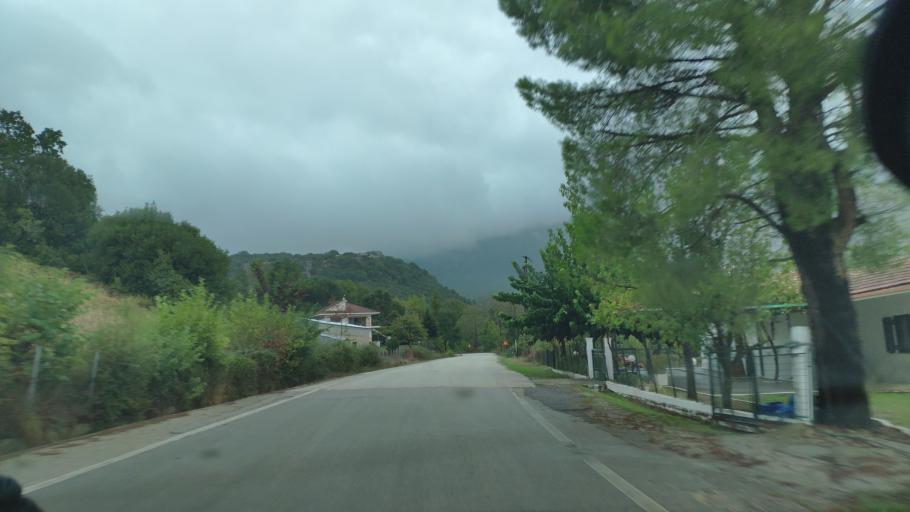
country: GR
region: West Greece
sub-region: Nomos Aitolias kai Akarnanias
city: Krikellos
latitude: 39.0188
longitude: 21.3072
